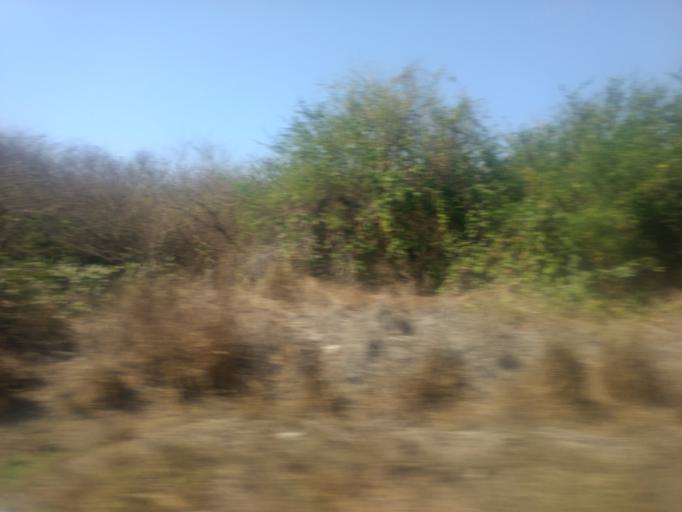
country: MX
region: Colima
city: El Colomo
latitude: 18.9929
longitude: -104.2339
